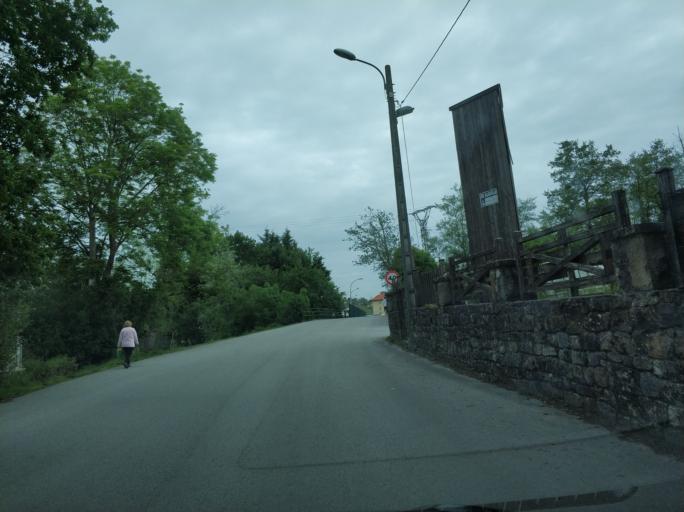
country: ES
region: Cantabria
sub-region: Provincia de Cantabria
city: Santa Maria de Cayon
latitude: 43.3193
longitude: -3.8563
